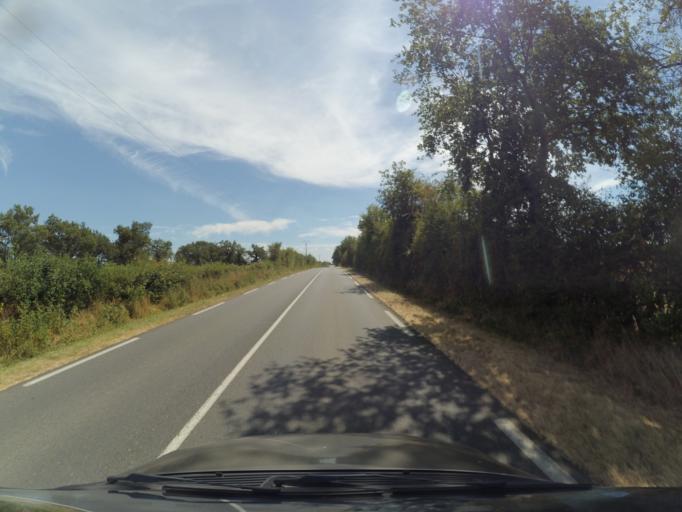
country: FR
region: Poitou-Charentes
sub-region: Departement de la Vienne
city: Availles-Limouzine
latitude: 46.1032
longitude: 0.5797
